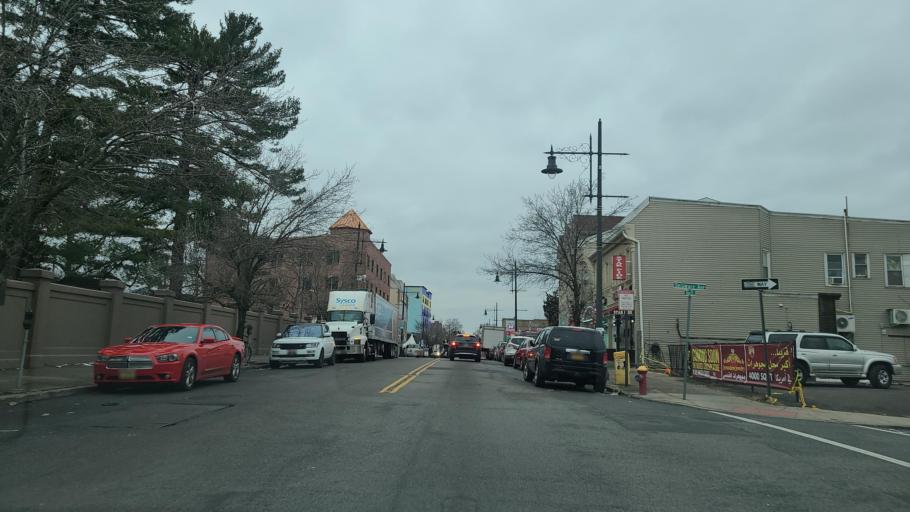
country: US
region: New Jersey
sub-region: Passaic County
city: Paterson
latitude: 40.8919
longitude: -74.1567
